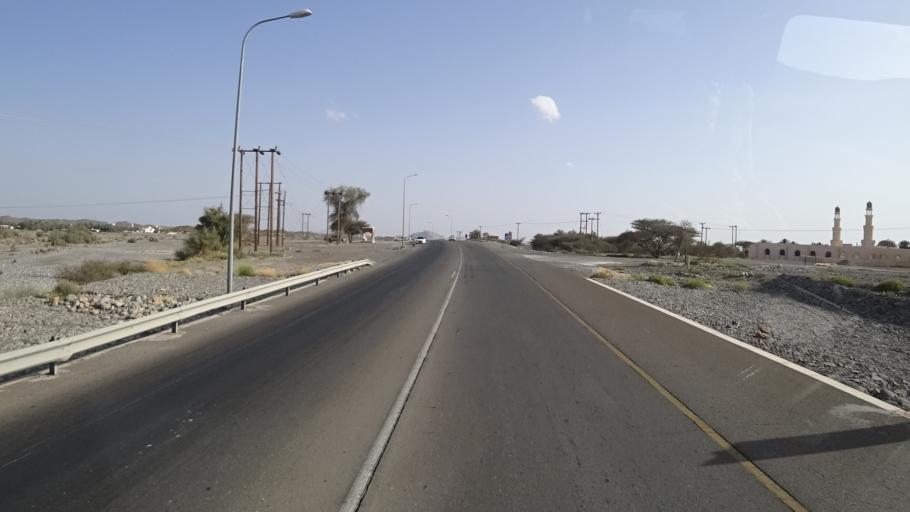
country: OM
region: Muhafazat ad Dakhiliyah
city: Izki
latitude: 22.8831
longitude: 57.7534
